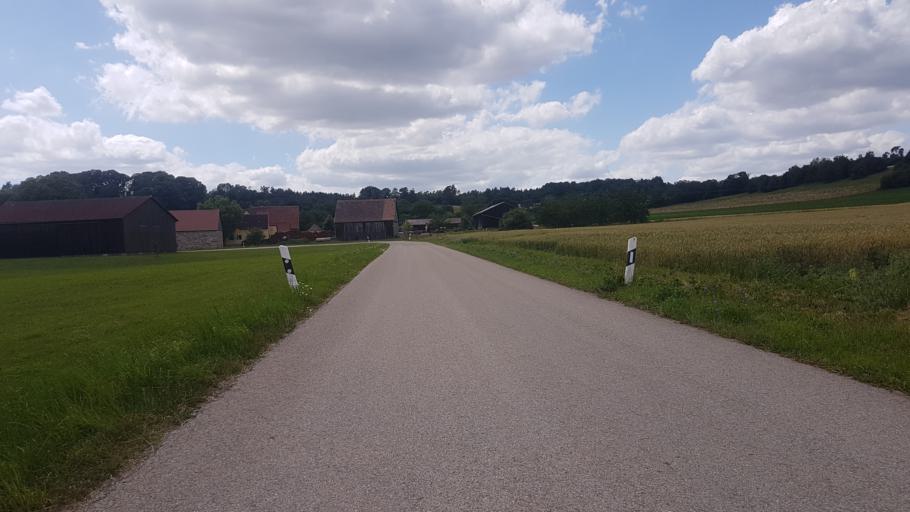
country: DE
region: Bavaria
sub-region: Regierungsbezirk Mittelfranken
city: Geslau
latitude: 49.3641
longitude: 10.2743
